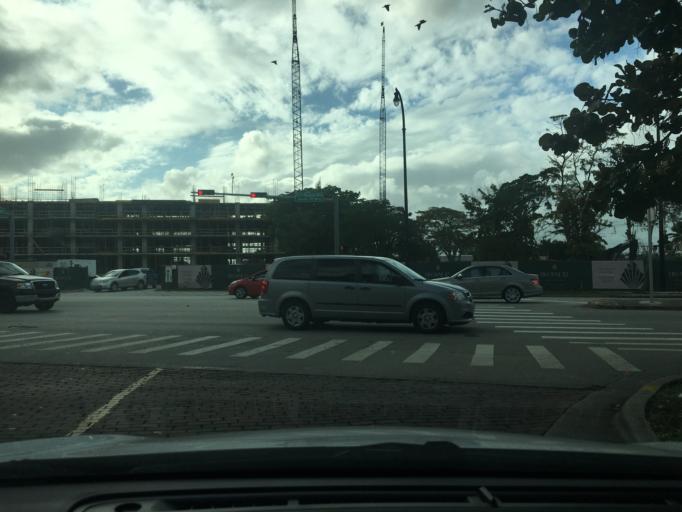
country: US
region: Florida
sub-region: Miami-Dade County
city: Biscayne Park
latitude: 25.8796
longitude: -80.1671
